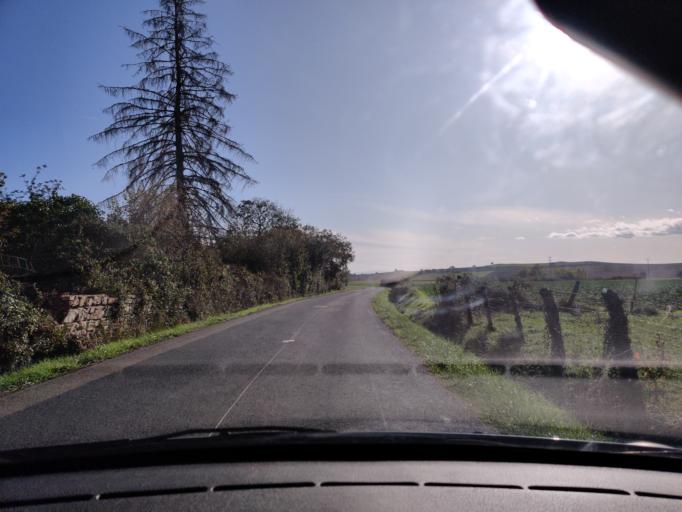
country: FR
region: Auvergne
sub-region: Departement du Puy-de-Dome
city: Aigueperse
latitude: 46.0399
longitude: 3.1390
